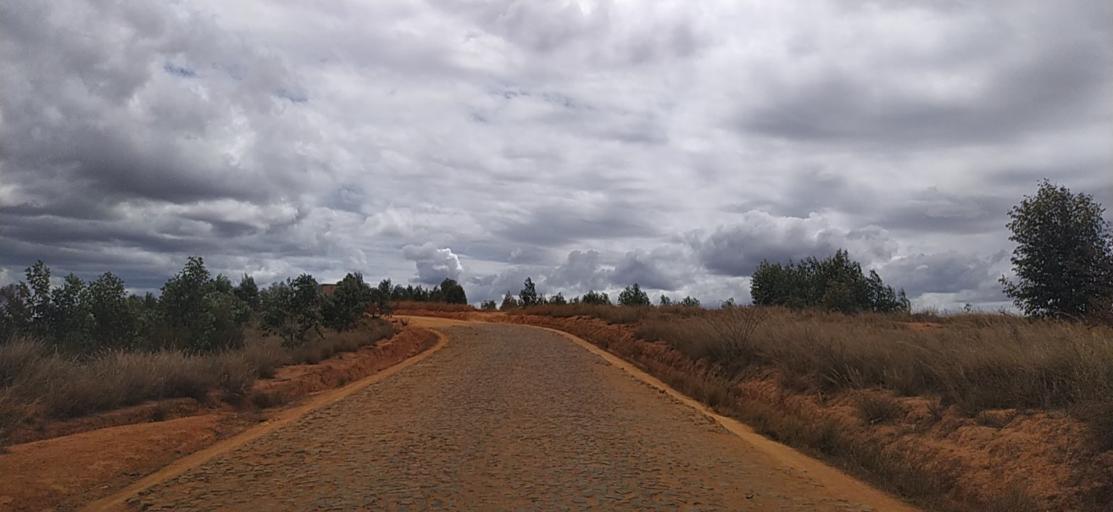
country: MG
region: Alaotra Mangoro
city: Ambatondrazaka
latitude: -18.0567
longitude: 48.2547
